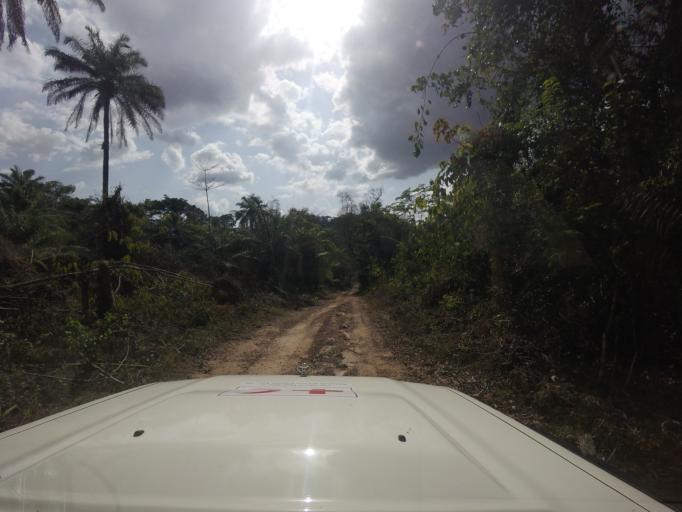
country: LR
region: Lofa
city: Voinjama
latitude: 8.3920
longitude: -9.6203
